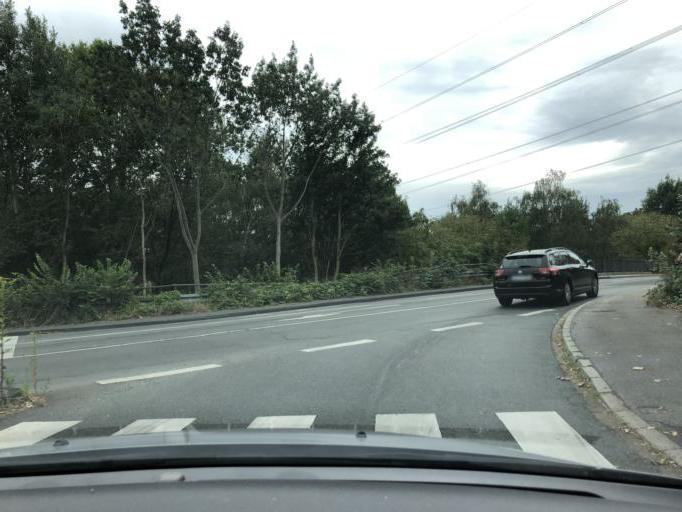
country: DE
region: North Rhine-Westphalia
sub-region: Regierungsbezirk Munster
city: Bottrop
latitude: 51.4952
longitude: 6.9514
